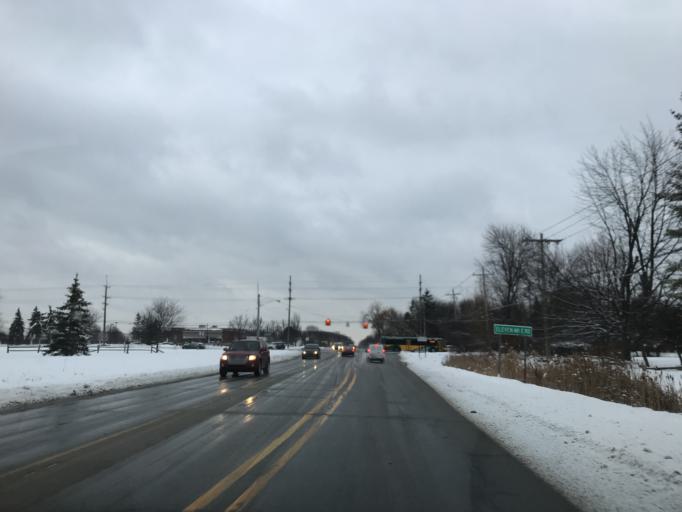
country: US
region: Michigan
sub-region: Oakland County
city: Franklin
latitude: 42.4867
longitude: -83.3190
